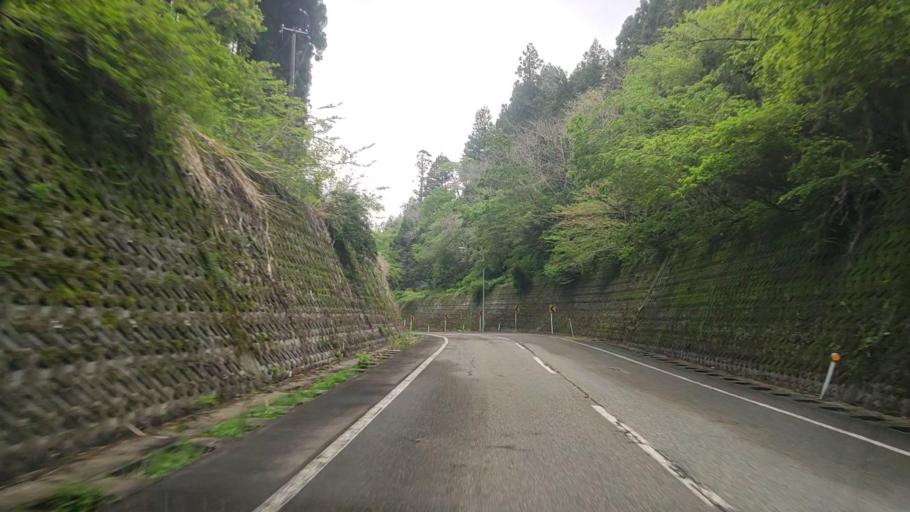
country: JP
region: Niigata
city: Gosen
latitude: 37.7131
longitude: 139.1109
